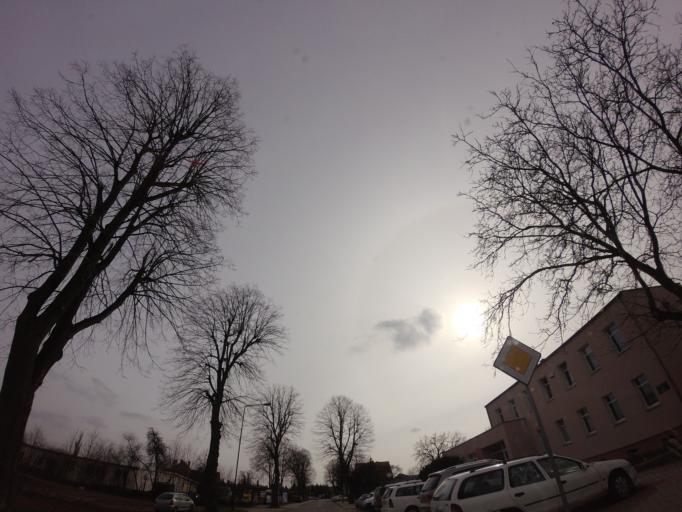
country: PL
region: West Pomeranian Voivodeship
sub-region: Powiat drawski
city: Drawsko Pomorskie
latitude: 53.5239
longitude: 15.8159
